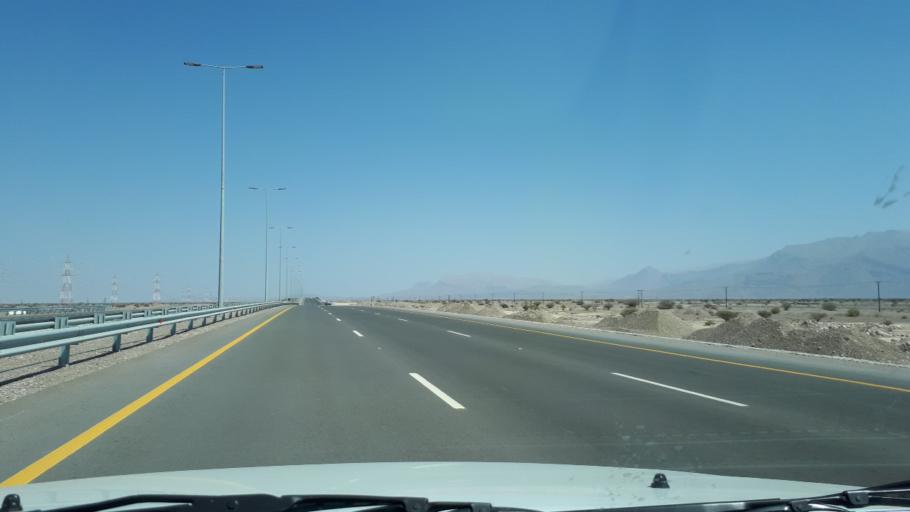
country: OM
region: Ash Sharqiyah
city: Badiyah
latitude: 22.3130
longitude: 59.1397
